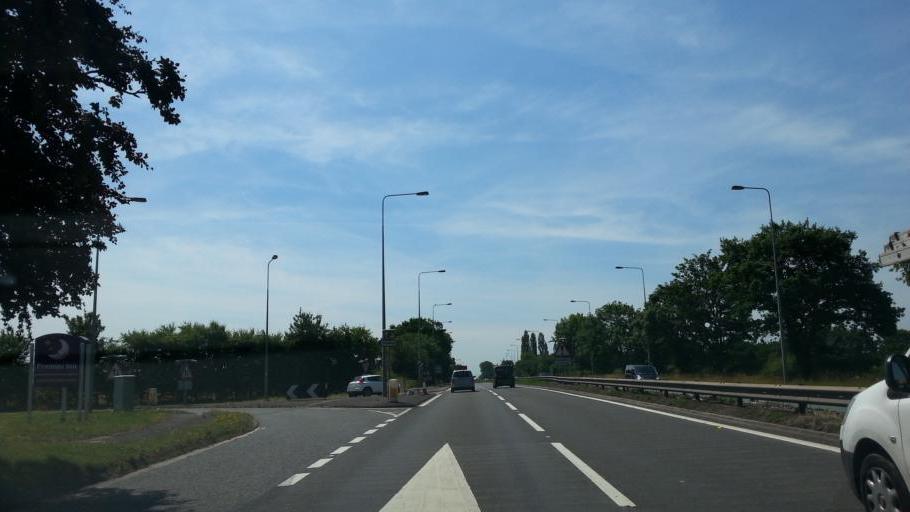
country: GB
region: England
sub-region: Staffordshire
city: Alrewas
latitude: 52.7141
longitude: -1.7622
